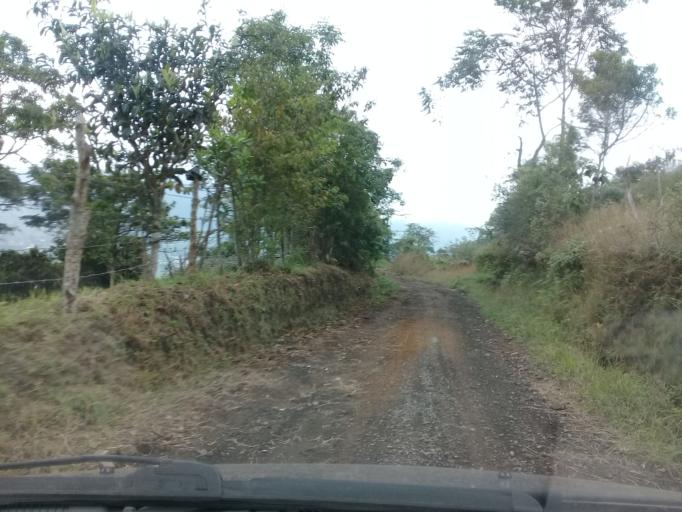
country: CO
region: Cundinamarca
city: Viani
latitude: 4.8413
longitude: -74.5534
